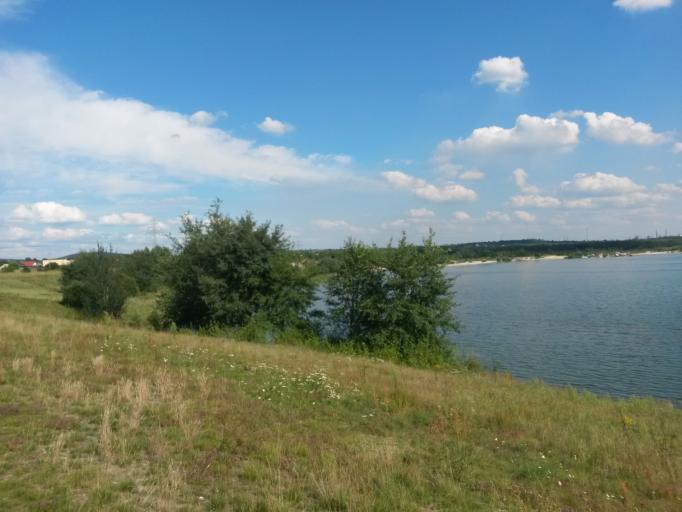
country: PL
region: Silesian Voivodeship
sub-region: Powiat bedzinski
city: Sarnow
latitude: 50.4066
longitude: 19.2051
